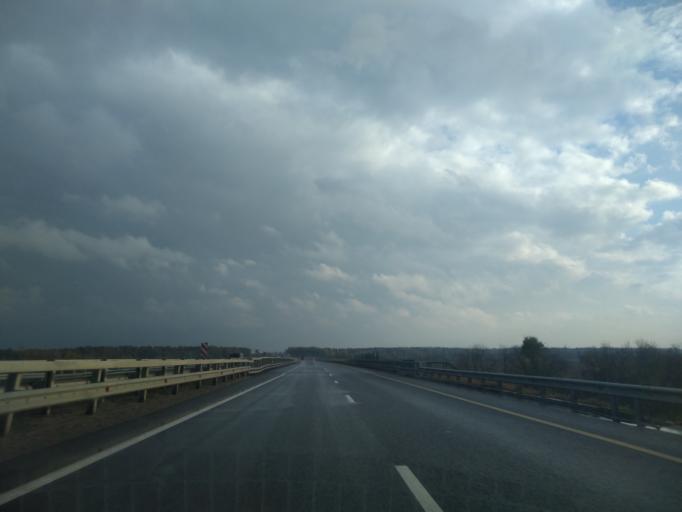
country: RU
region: Lipetsk
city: Yelets
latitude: 52.6045
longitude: 38.6672
